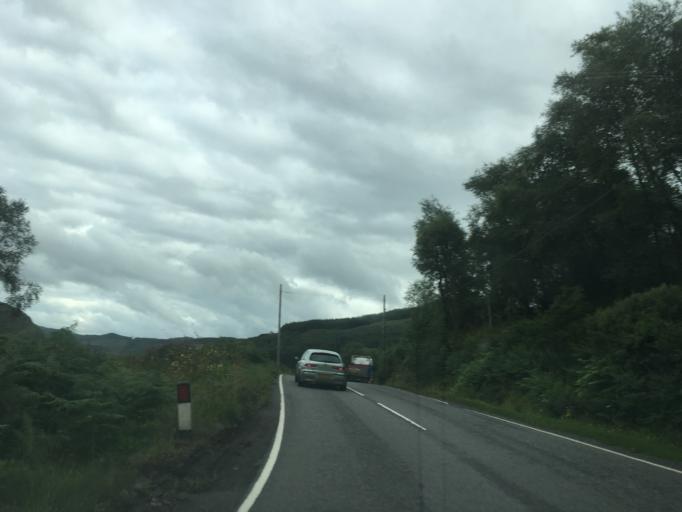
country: GB
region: Scotland
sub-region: Argyll and Bute
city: Oban
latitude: 56.3019
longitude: -5.4657
